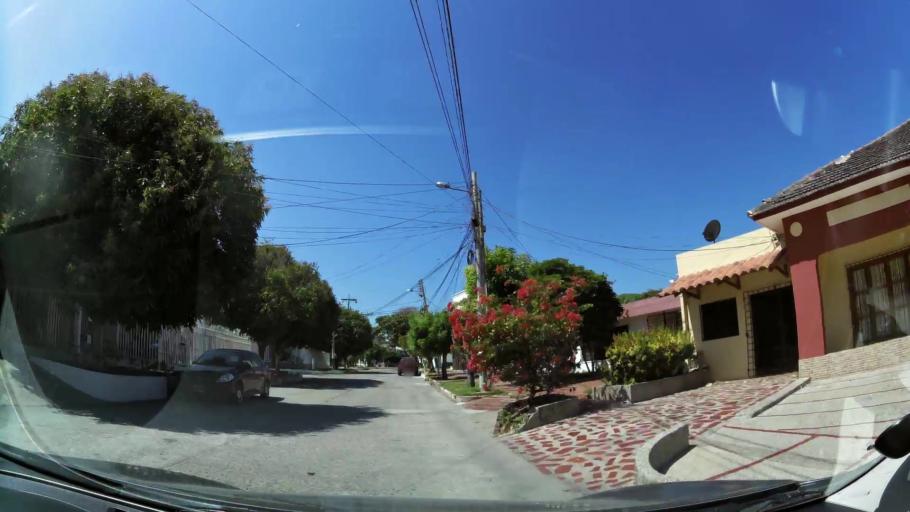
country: CO
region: Atlantico
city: Barranquilla
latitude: 11.0016
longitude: -74.7930
